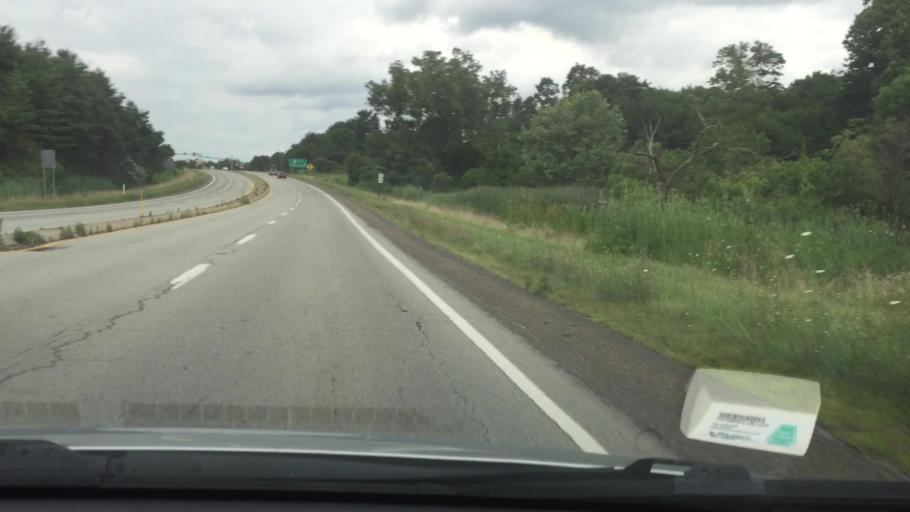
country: US
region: Pennsylvania
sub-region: Armstrong County
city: Freeport
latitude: 40.6882
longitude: -79.7038
